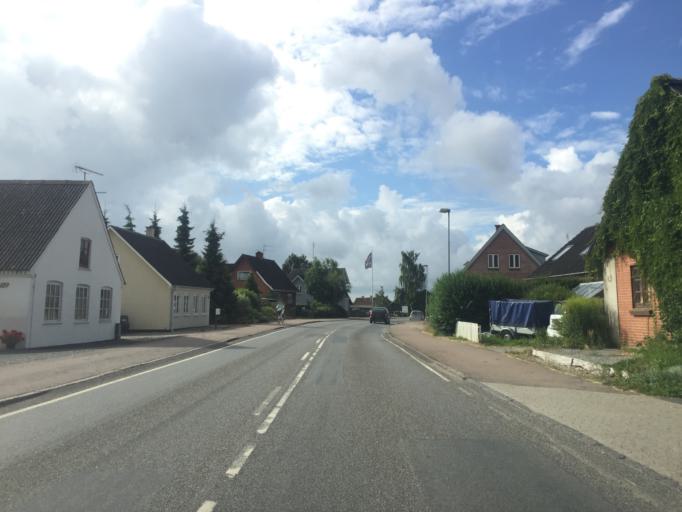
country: DK
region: South Denmark
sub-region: Svendborg Kommune
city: Thuro By
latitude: 55.1070
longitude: 10.7135
